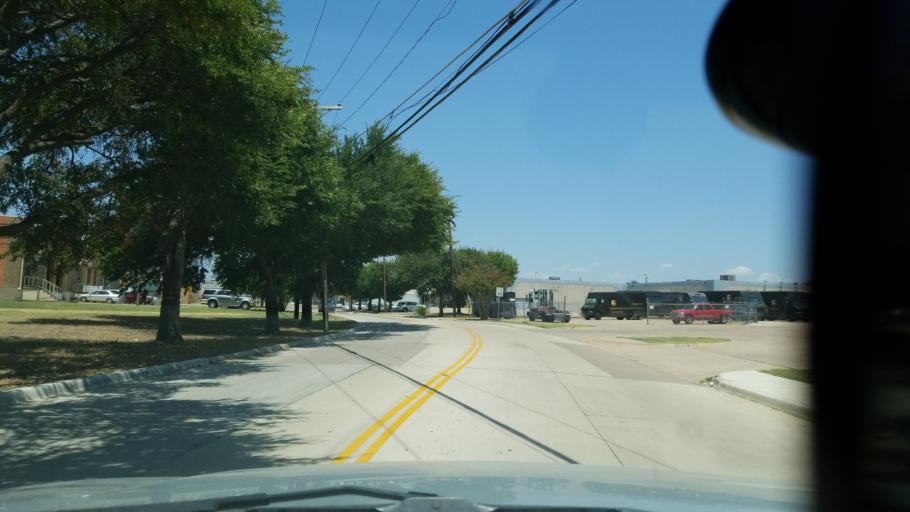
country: US
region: Texas
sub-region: Dallas County
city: Farmers Branch
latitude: 32.9043
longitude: -96.8868
